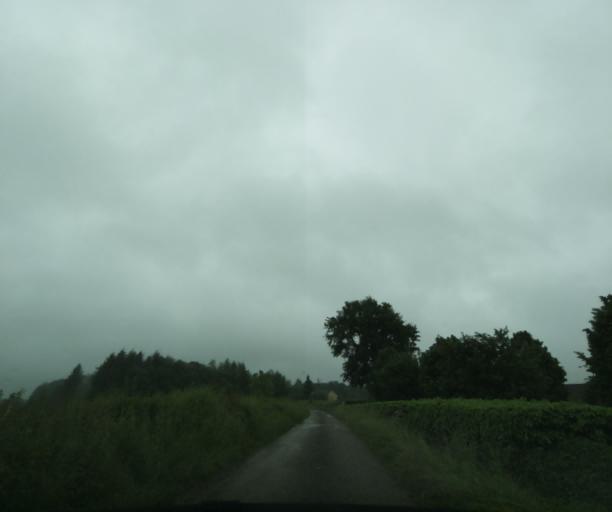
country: FR
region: Bourgogne
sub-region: Departement de Saone-et-Loire
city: Charolles
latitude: 46.3858
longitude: 4.3349
